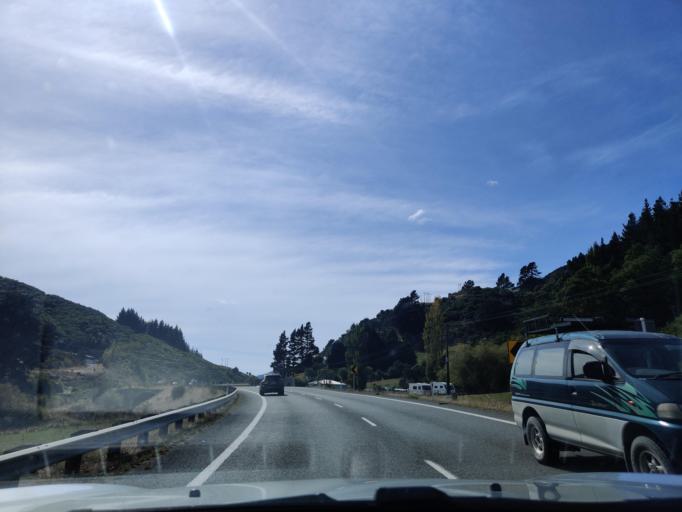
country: NZ
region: Marlborough
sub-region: Marlborough District
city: Picton
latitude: -41.3085
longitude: 173.9843
